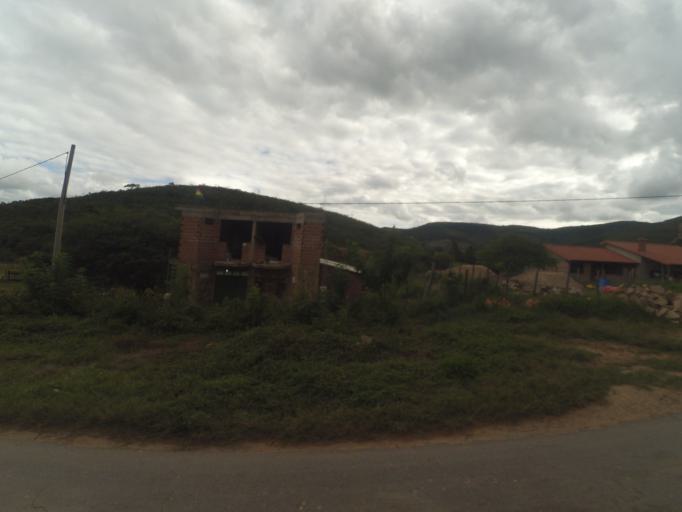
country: BO
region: Santa Cruz
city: Samaipata
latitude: -18.1703
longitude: -63.8313
